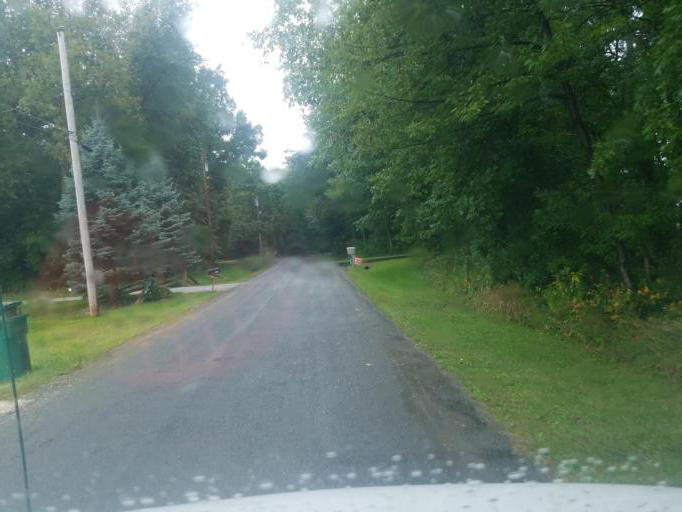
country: US
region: Ohio
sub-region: Medina County
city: Seville
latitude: 41.0304
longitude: -81.8148
